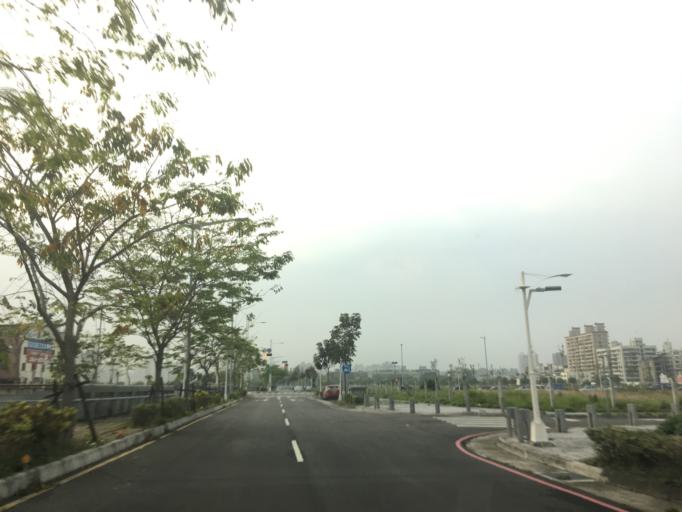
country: TW
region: Taiwan
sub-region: Taichung City
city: Taichung
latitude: 24.1909
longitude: 120.6699
